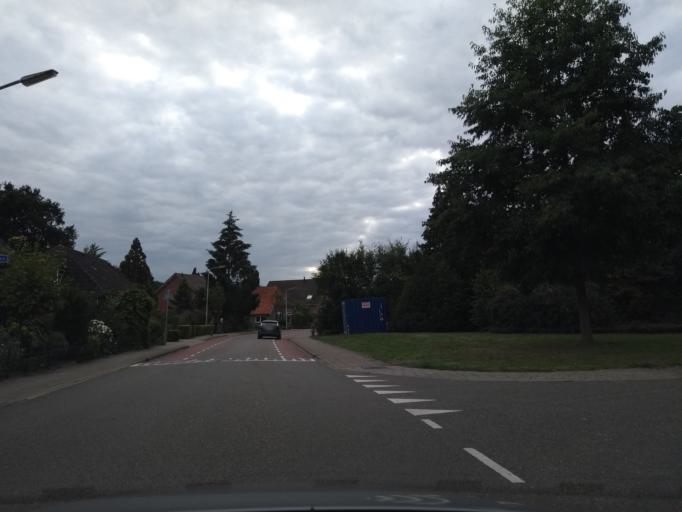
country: NL
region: Gelderland
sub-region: Gemeente Lochem
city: Barchem
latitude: 52.0893
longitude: 6.4543
